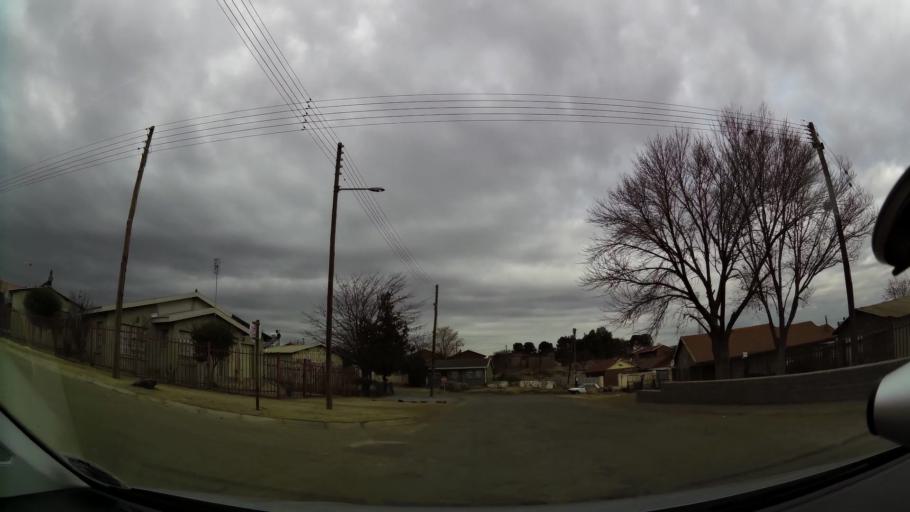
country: ZA
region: Orange Free State
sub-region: Fezile Dabi District Municipality
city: Kroonstad
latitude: -27.6489
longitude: 27.1825
